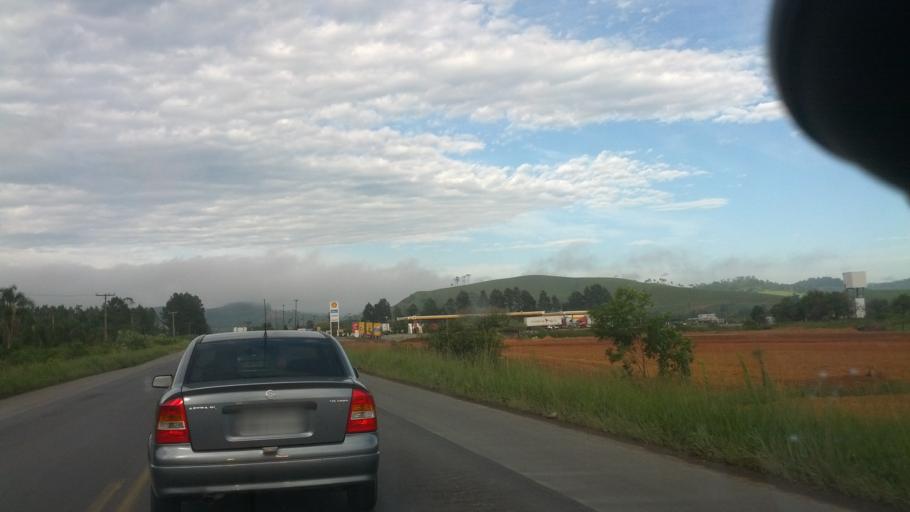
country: BR
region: Santa Catarina
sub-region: Otacilio Costa
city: Otacilio Costa
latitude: -27.2492
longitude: -49.9859
